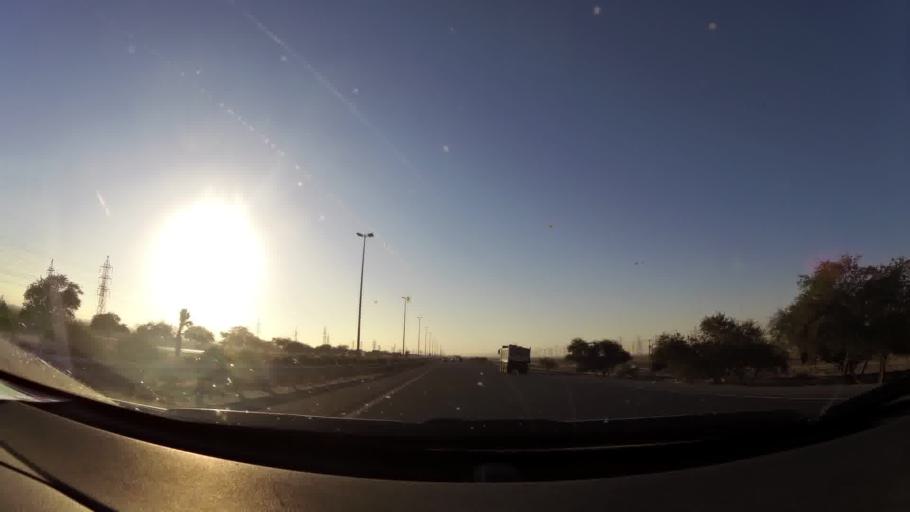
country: KW
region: Al Ahmadi
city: Al Fahahil
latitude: 28.8622
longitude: 48.2384
